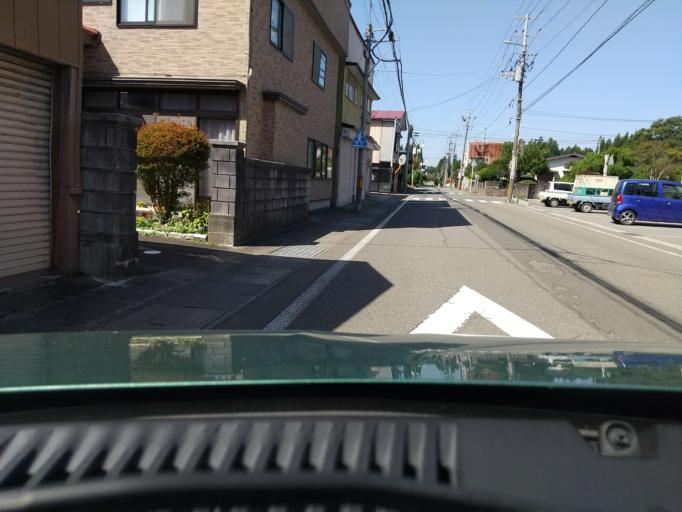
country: JP
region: Akita
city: Akita
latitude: 39.6178
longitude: 140.3204
